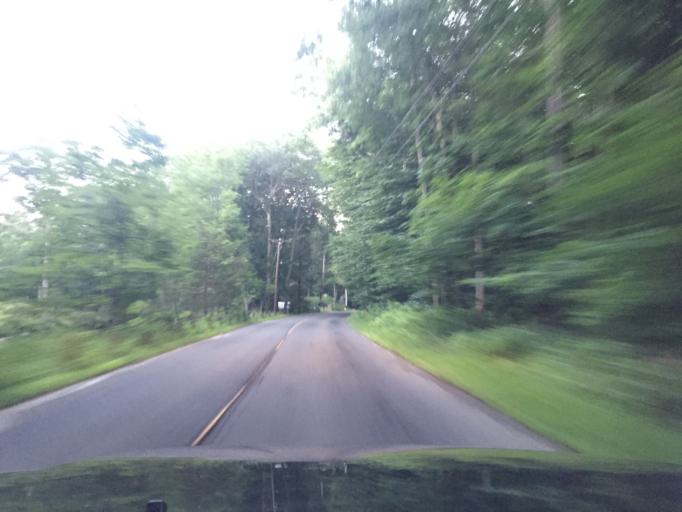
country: US
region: Connecticut
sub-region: Fairfield County
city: Newtown
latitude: 41.4116
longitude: -73.3660
